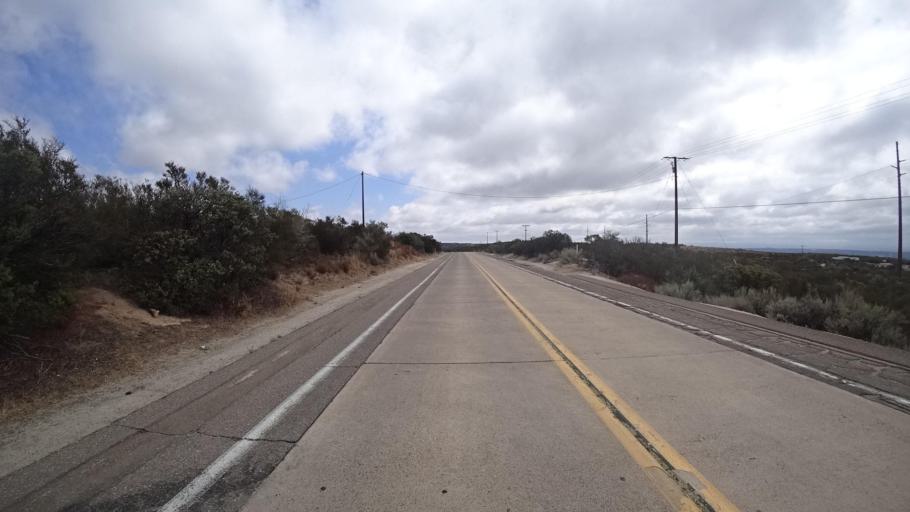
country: US
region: California
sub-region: San Diego County
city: Campo
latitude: 32.6980
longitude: -116.3529
